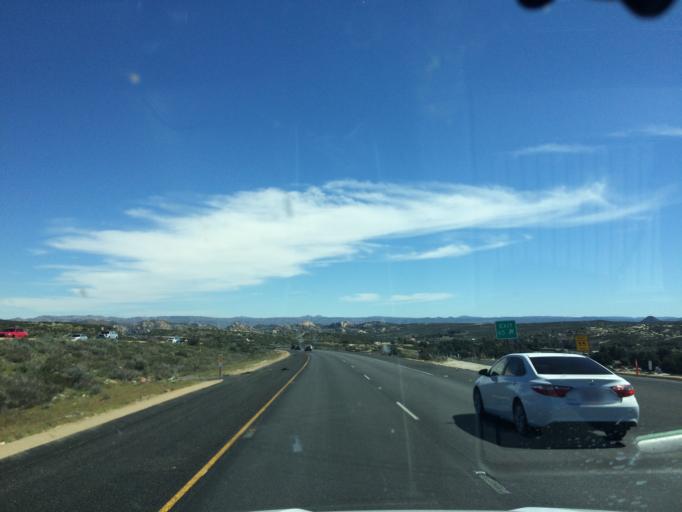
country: US
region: California
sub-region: San Diego County
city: Campo
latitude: 32.6792
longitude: -116.2948
